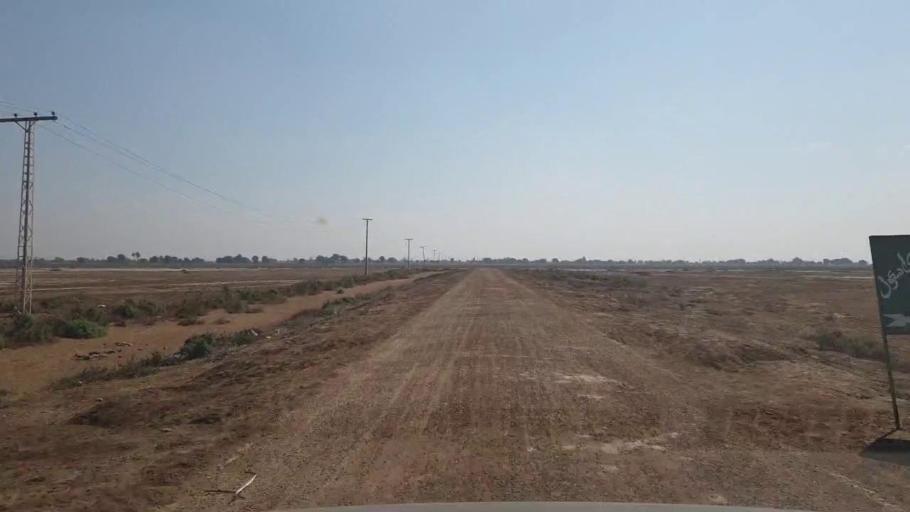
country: PK
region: Sindh
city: Digri
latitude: 25.2282
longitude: 69.2237
